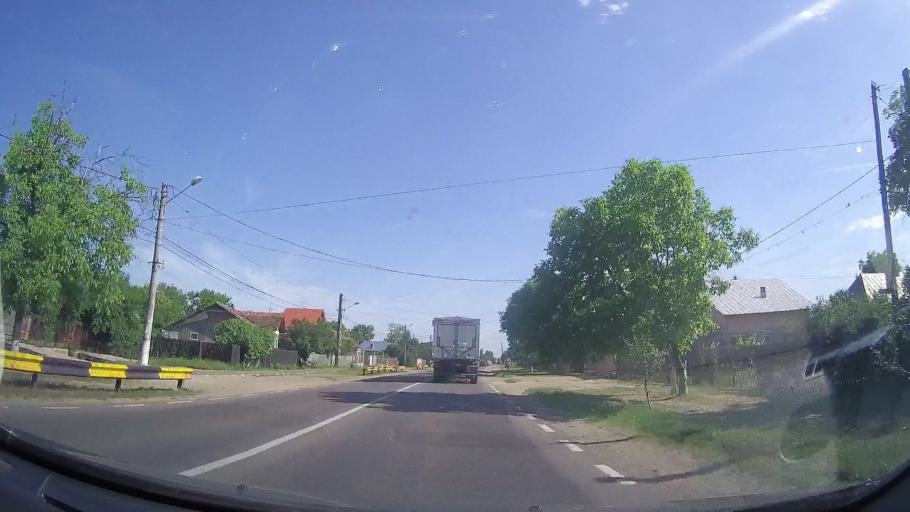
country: RO
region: Prahova
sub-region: Comuna Lipanesti
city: Sipotu
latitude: 45.0321
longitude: 26.0179
